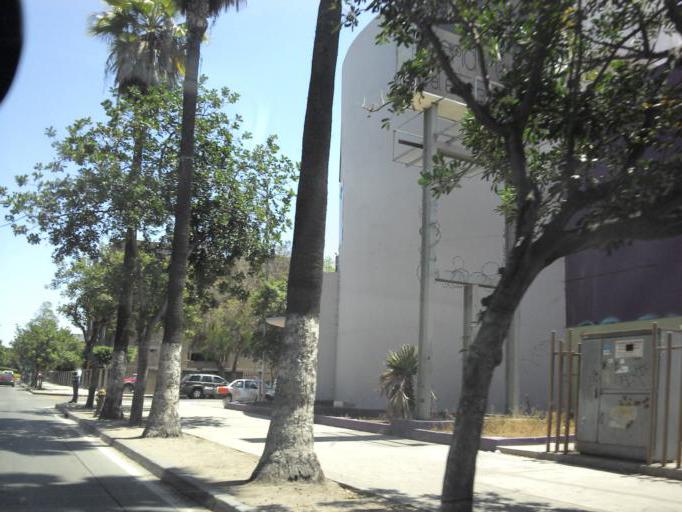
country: MX
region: Baja California
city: Tijuana
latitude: 32.5345
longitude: -117.0210
